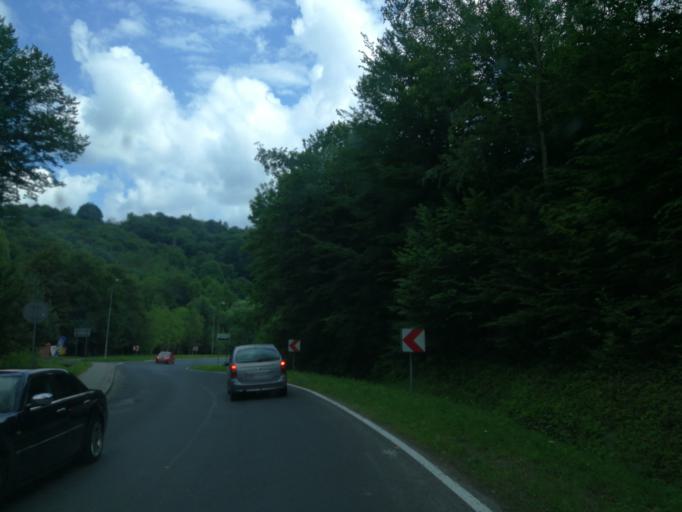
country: PL
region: Subcarpathian Voivodeship
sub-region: Powiat leski
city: Polanczyk
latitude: 49.4022
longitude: 22.4593
